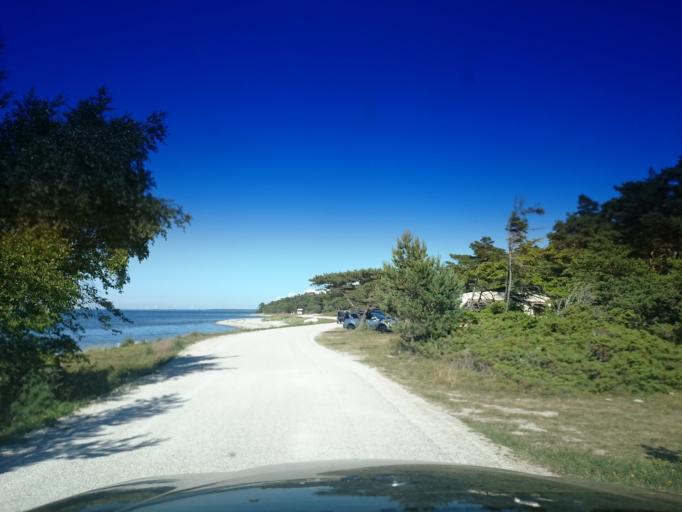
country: SE
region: Gotland
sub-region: Gotland
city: Klintehamn
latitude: 57.2947
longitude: 18.1262
